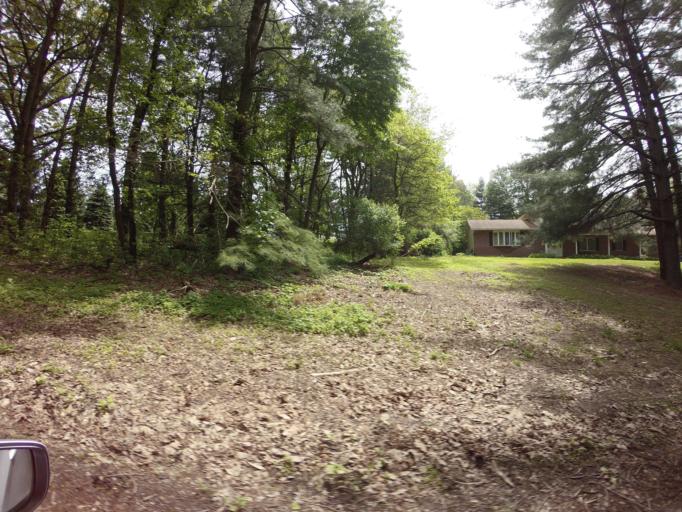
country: US
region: Maryland
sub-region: Carroll County
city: Eldersburg
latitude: 39.4756
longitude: -77.0242
